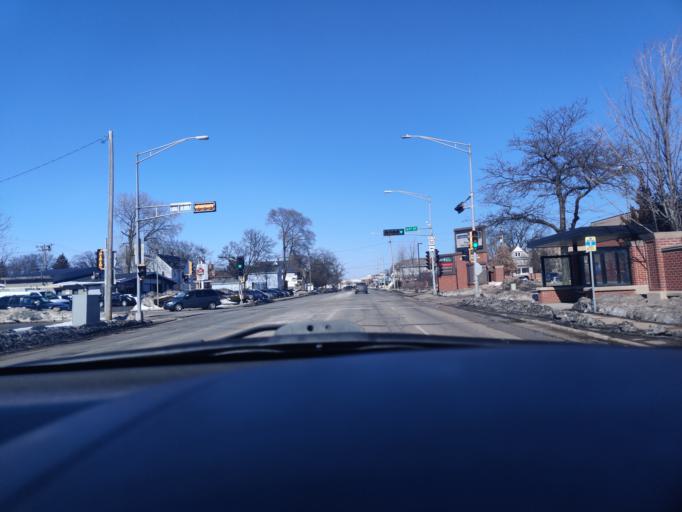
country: US
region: Wisconsin
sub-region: Kenosha County
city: Kenosha
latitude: 42.5775
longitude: -87.8215
